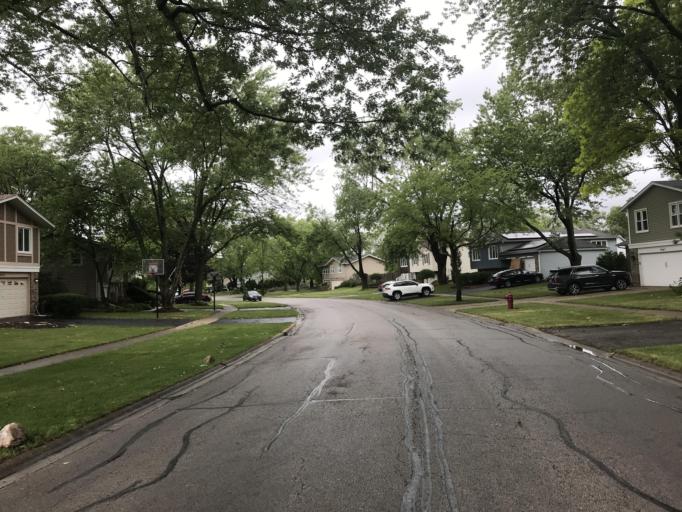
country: US
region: Illinois
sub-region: DuPage County
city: Woodridge
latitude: 41.7412
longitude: -88.0539
